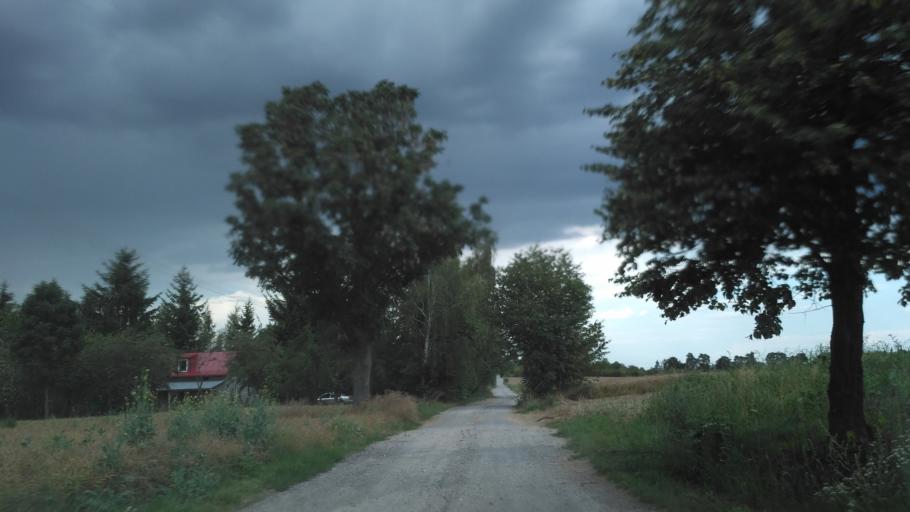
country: PL
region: Lublin Voivodeship
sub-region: Powiat leczynski
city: Milejow
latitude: 51.2051
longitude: 22.8695
